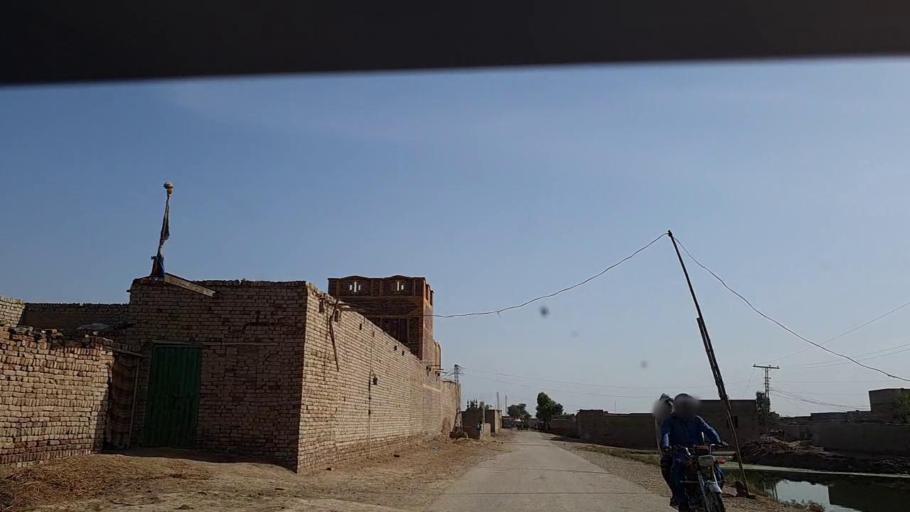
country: PK
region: Sindh
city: Phulji
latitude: 26.9928
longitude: 67.6645
